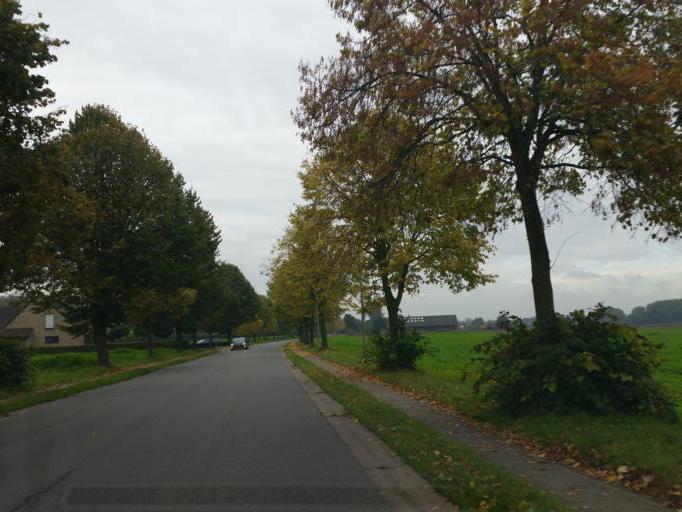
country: BE
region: Flanders
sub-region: Provincie Vlaams-Brabant
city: Steenokkerzeel
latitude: 50.9229
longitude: 4.4939
